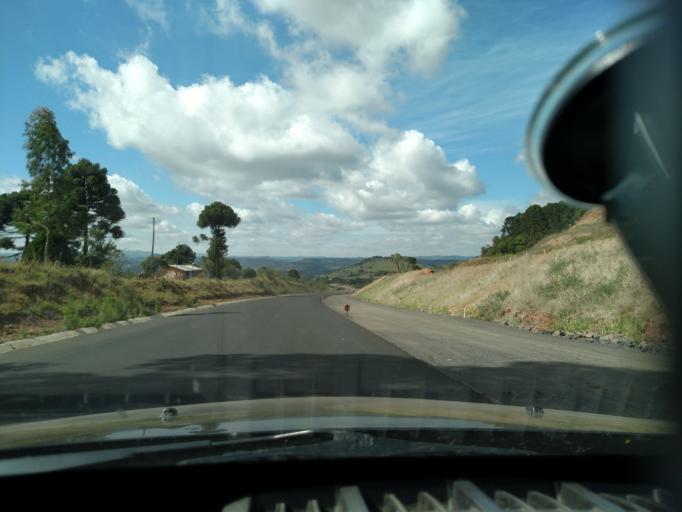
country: BR
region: Santa Catarina
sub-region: Sao Joaquim
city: Sao Joaquim
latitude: -28.0628
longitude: -50.0734
